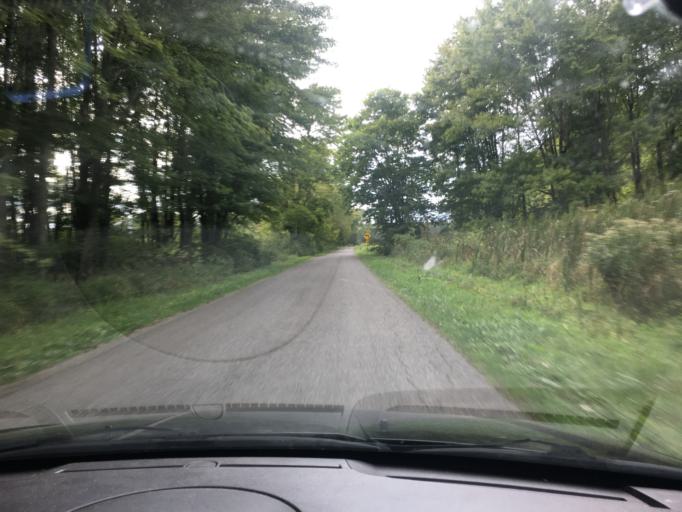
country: US
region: Ohio
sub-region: Logan County
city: West Liberty
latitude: 40.2573
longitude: -83.7413
